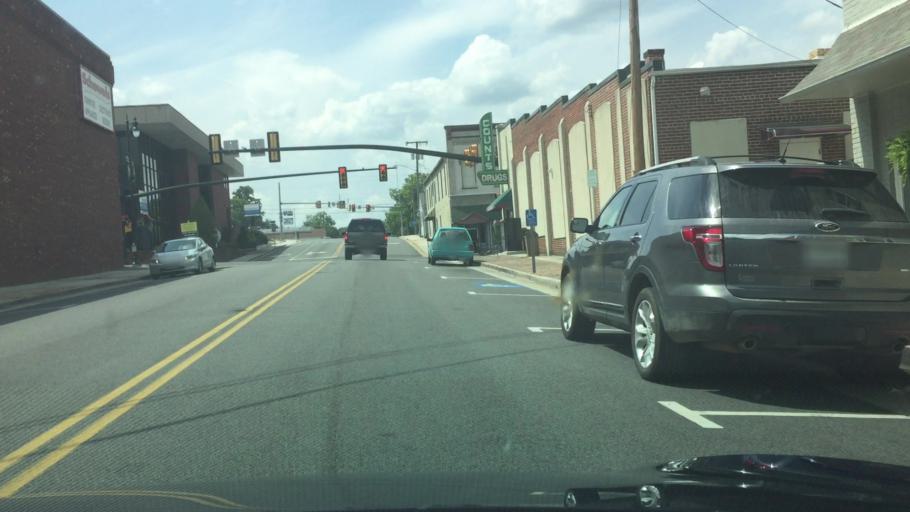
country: US
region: Virginia
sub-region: Wythe County
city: Wytheville
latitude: 36.9482
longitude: -81.0847
